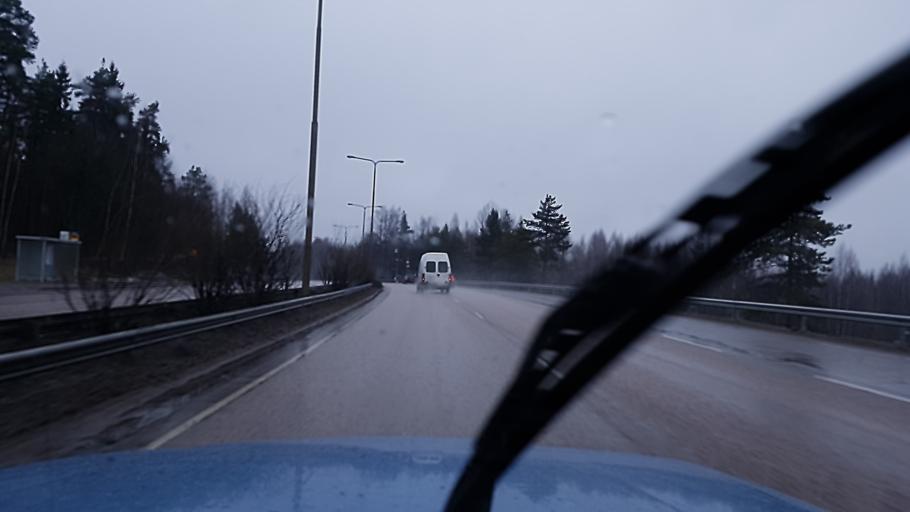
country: FI
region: Uusimaa
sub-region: Helsinki
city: Teekkarikylae
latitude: 60.2702
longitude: 24.8749
